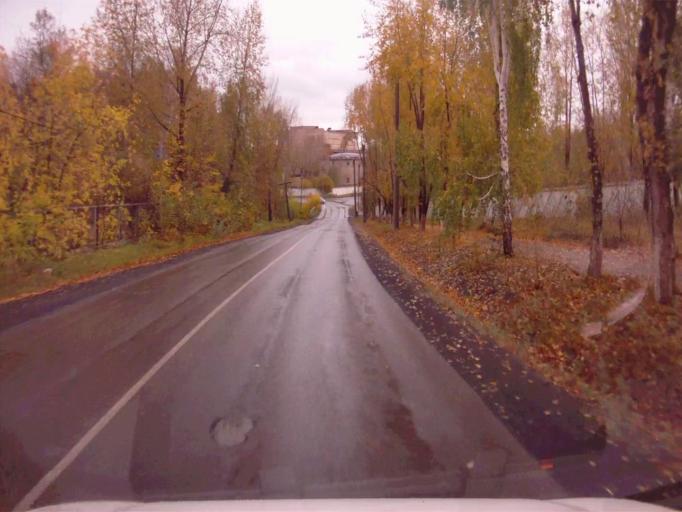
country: RU
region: Chelyabinsk
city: Verkhniy Ufaley
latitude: 56.0424
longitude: 60.2495
